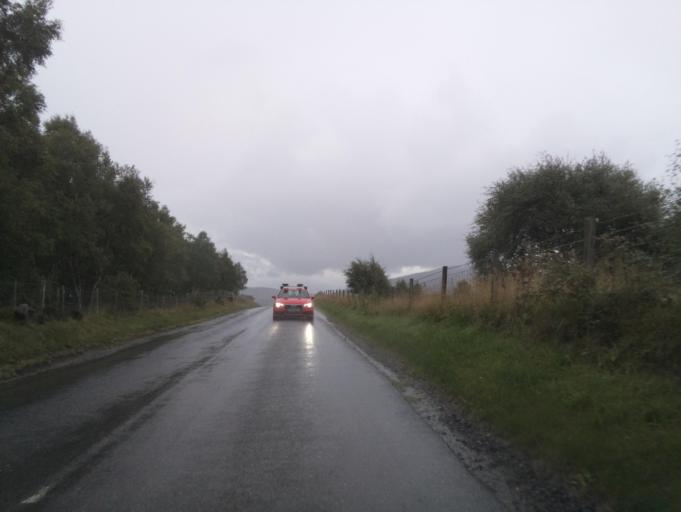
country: GB
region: Scotland
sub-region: Highland
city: Grantown on Spey
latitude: 57.3135
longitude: -3.5869
